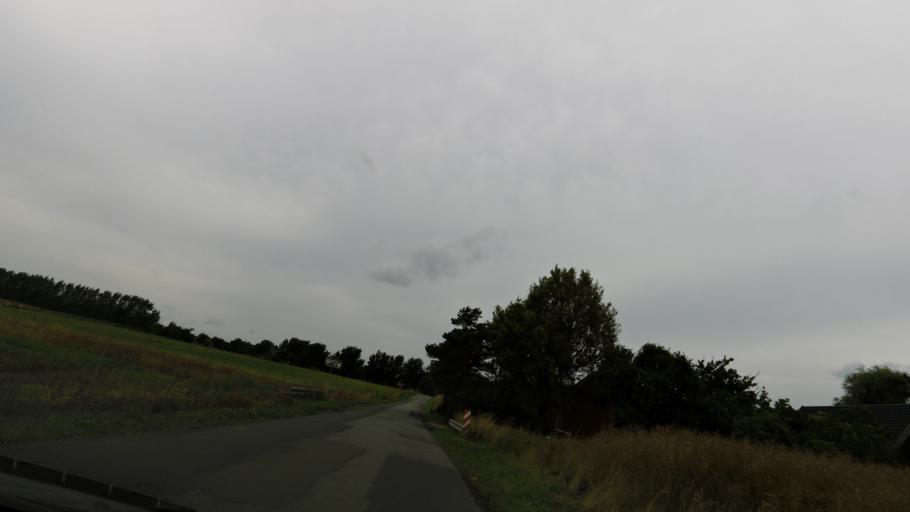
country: DK
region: South Denmark
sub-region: Nordfyns Kommune
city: Otterup
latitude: 55.5794
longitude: 10.3947
